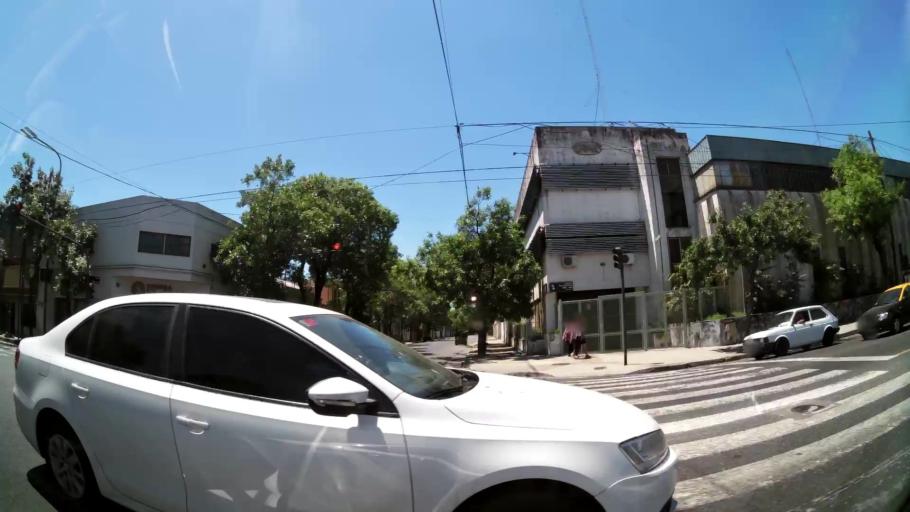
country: AR
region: Buenos Aires
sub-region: Partido de Avellaneda
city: Avellaneda
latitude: -34.6570
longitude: -58.3885
